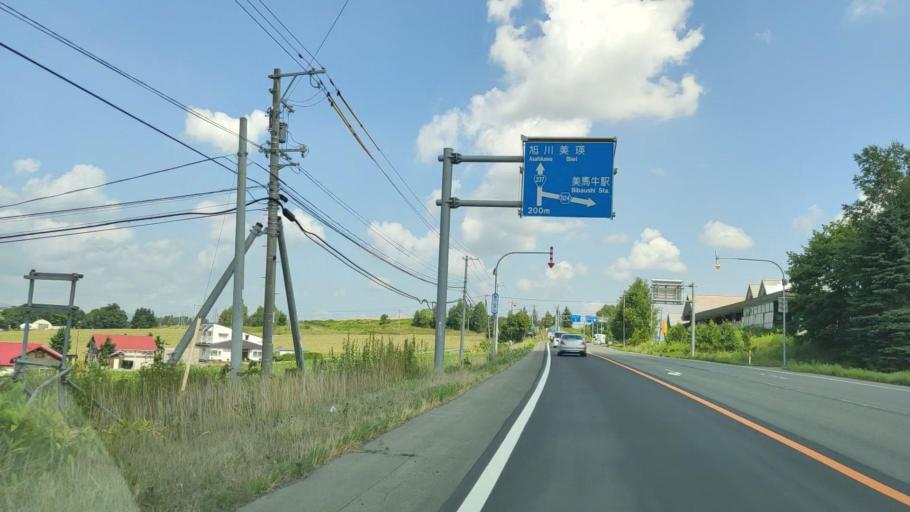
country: JP
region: Hokkaido
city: Shimo-furano
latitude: 43.5434
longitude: 142.4386
